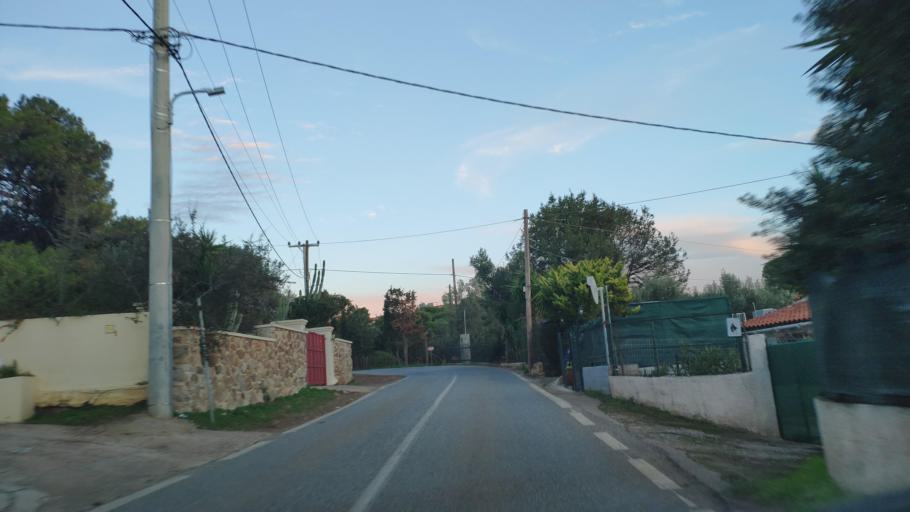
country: GR
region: Attica
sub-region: Nomarchia Anatolikis Attikis
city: Lavrio
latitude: 37.6710
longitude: 24.0441
